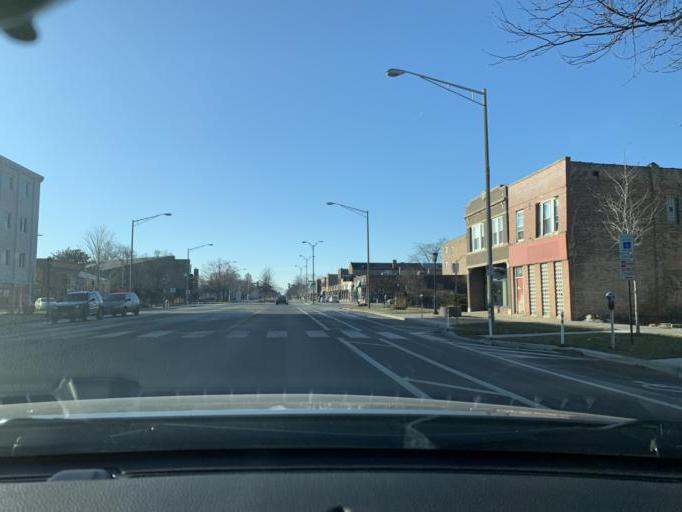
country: US
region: Illinois
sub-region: Cook County
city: Oak Park
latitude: 41.8801
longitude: -87.7770
